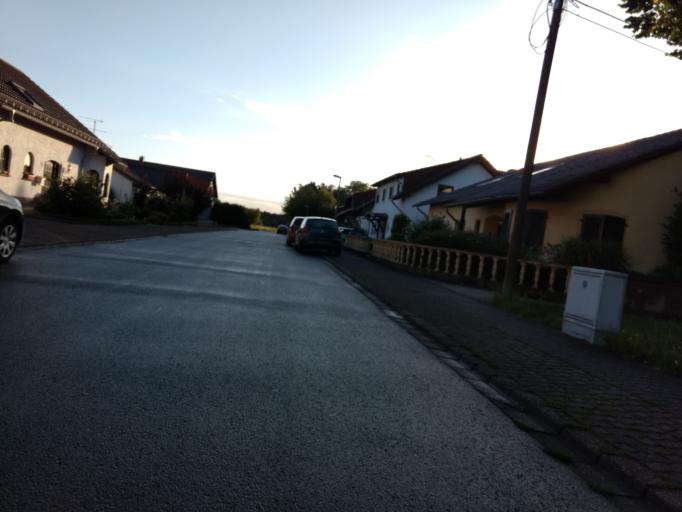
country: DE
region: Saarland
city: Nalbach
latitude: 49.3827
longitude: 6.7536
